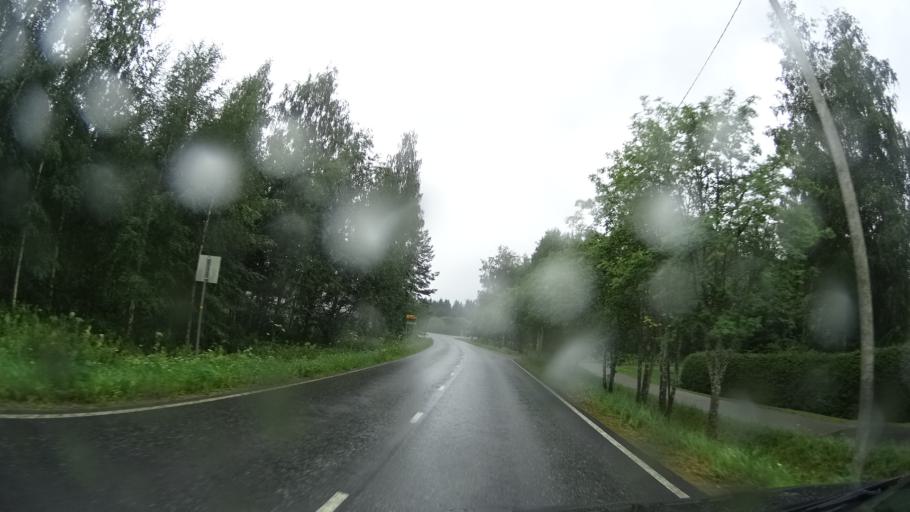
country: FI
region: North Karelia
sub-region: Keski-Karjala
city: Raeaekkylae
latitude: 62.3158
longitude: 29.6073
